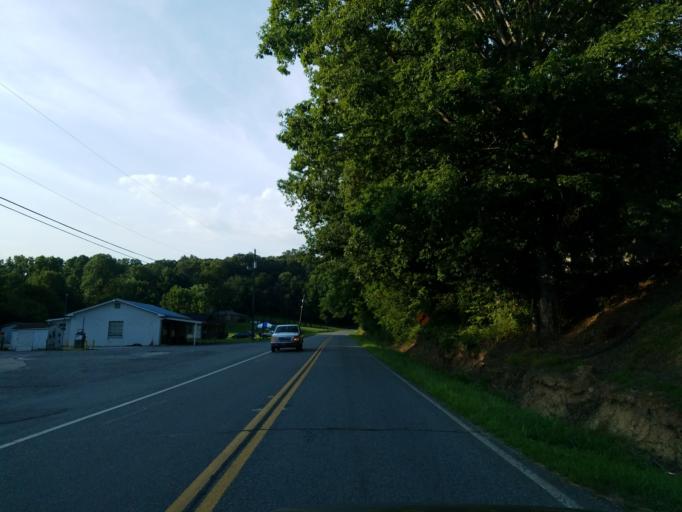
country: US
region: Georgia
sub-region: Gilmer County
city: Ellijay
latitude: 34.6260
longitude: -84.5162
